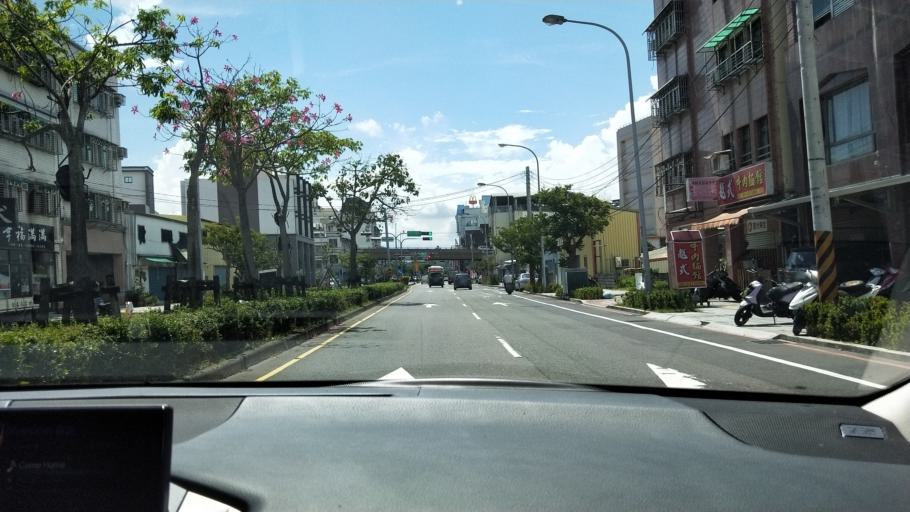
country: TW
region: Taiwan
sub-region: Yilan
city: Yilan
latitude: 24.7597
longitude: 121.7595
